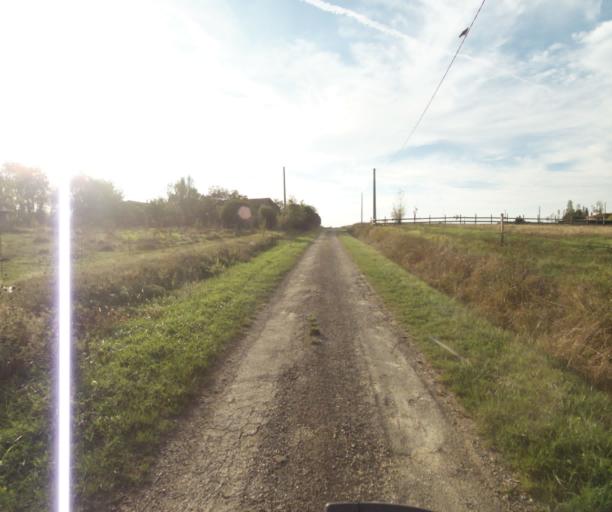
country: FR
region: Midi-Pyrenees
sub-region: Departement du Tarn-et-Garonne
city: Finhan
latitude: 43.9188
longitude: 1.1364
